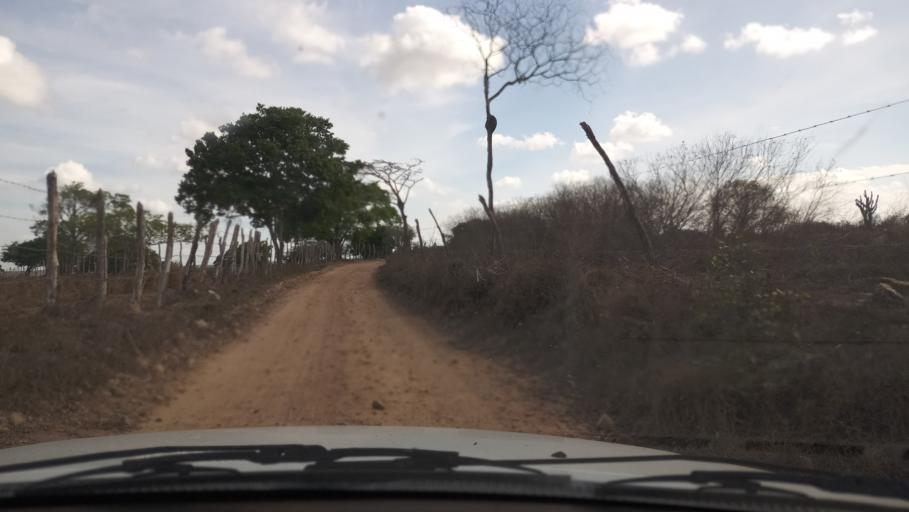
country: BR
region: Rio Grande do Norte
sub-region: Goianinha
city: Goianinha
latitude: -6.3161
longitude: -35.3075
